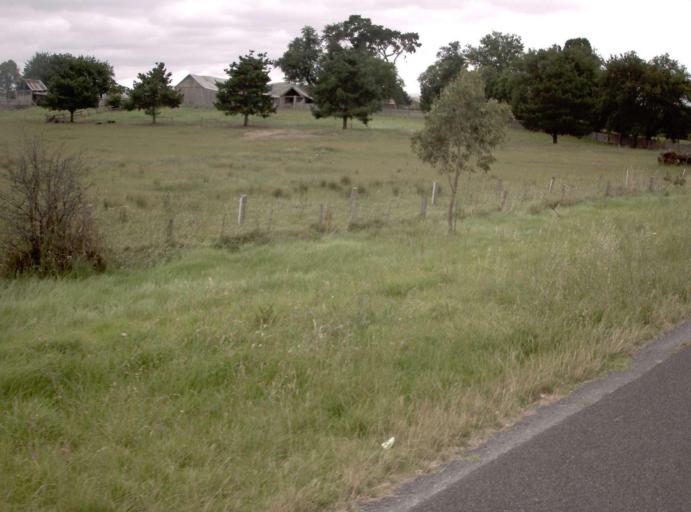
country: AU
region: Victoria
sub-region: Yarra Ranges
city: Yarra Glen
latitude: -37.6496
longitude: 145.3853
